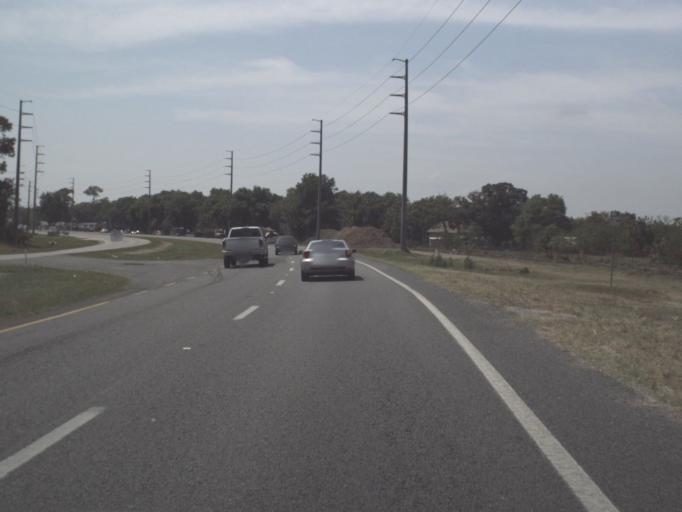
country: US
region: Florida
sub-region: Lake County
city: Umatilla
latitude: 28.9018
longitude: -81.6855
